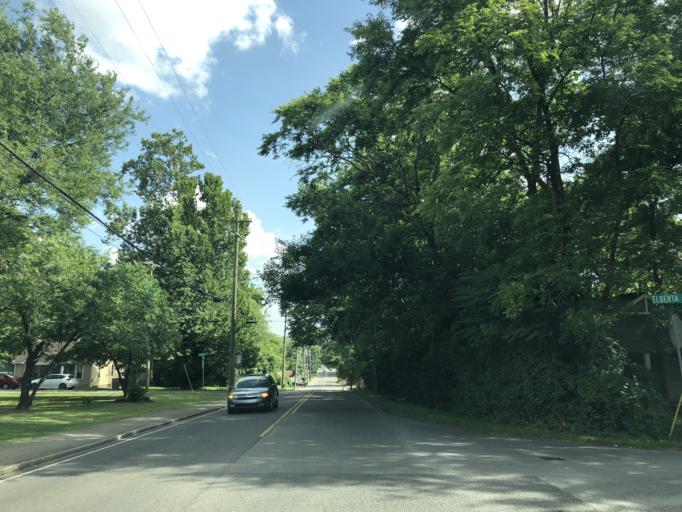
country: US
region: Tennessee
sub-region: Davidson County
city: Oak Hill
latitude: 36.1187
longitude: -86.7432
